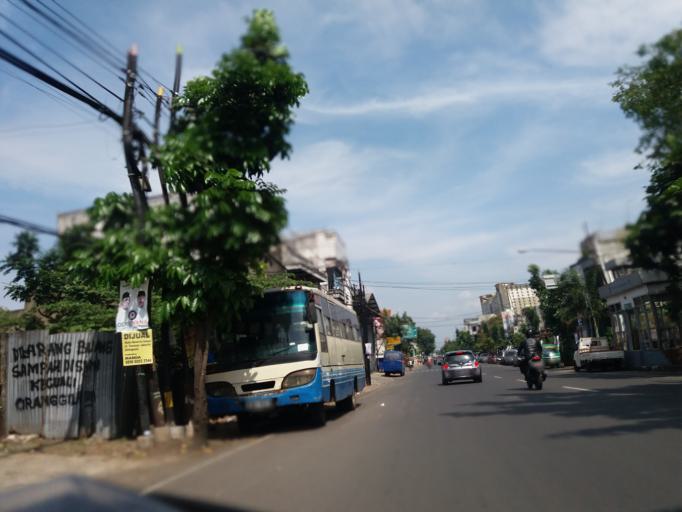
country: ID
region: West Java
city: Bandung
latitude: -6.9049
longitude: 107.6505
